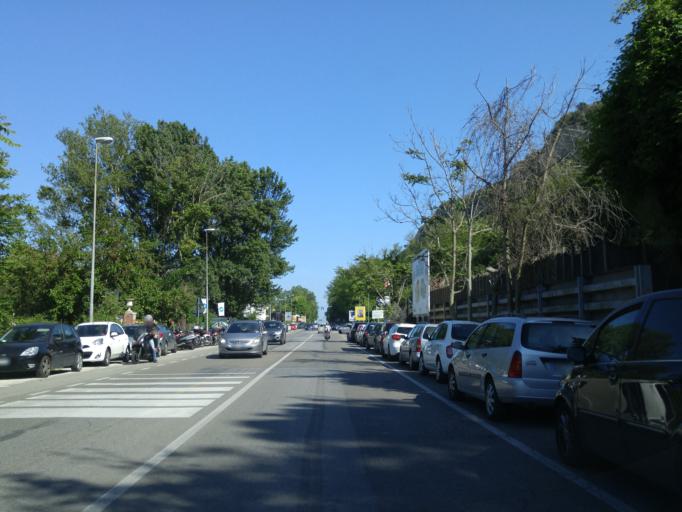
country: IT
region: The Marches
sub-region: Provincia di Pesaro e Urbino
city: Pesaro
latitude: 43.9045
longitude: 12.9282
